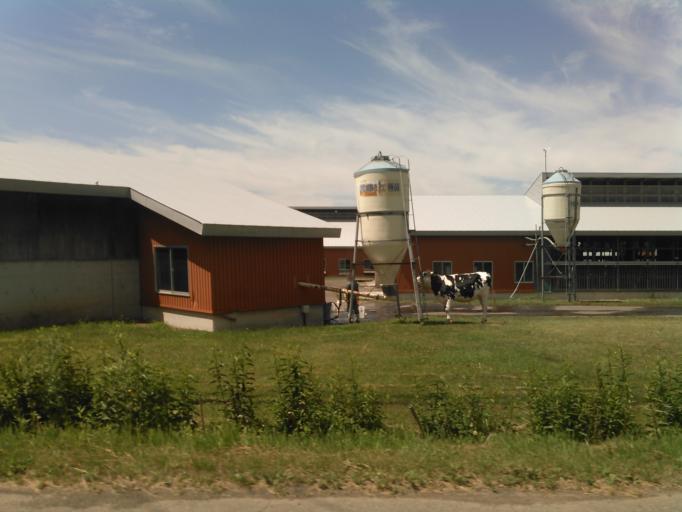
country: JP
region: Hokkaido
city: Ebetsu
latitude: 43.0757
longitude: 141.5111
